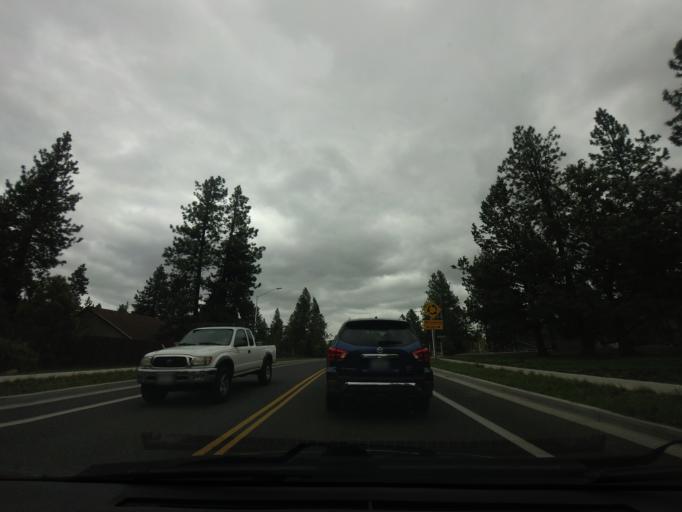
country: US
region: Oregon
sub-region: Deschutes County
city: Bend
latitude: 44.0213
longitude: -121.3283
